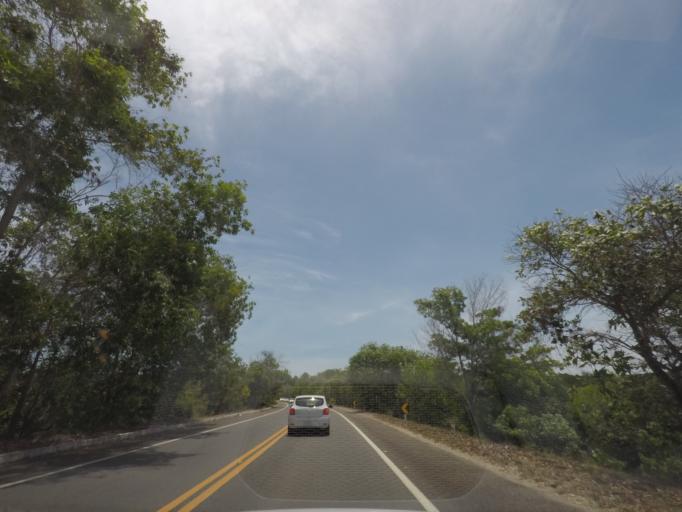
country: BR
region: Bahia
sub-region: Mata De Sao Joao
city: Mata de Sao Joao
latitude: -12.4030
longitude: -37.9247
